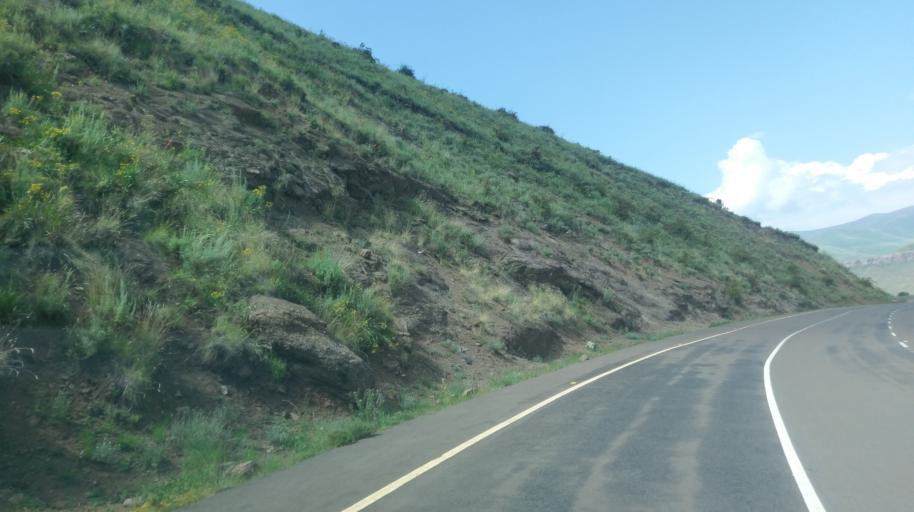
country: LS
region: Thaba-Tseka
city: Thaba-Tseka
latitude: -29.1491
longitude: 28.4860
